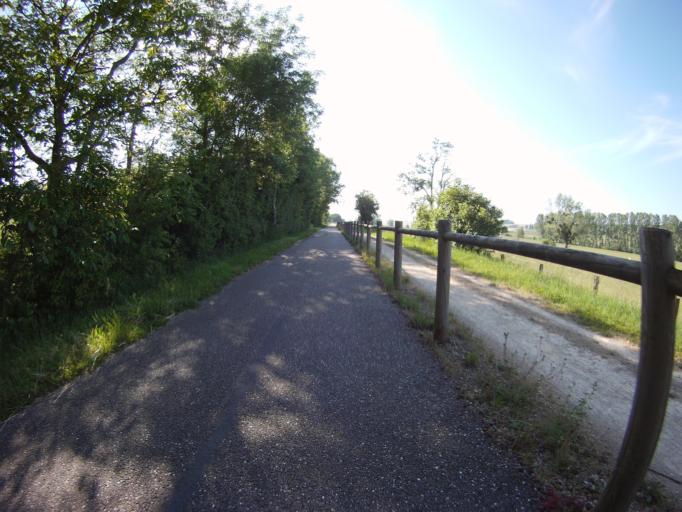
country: FR
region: Lorraine
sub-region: Departement de Meurthe-et-Moselle
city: Eulmont
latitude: 48.7397
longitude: 6.2508
